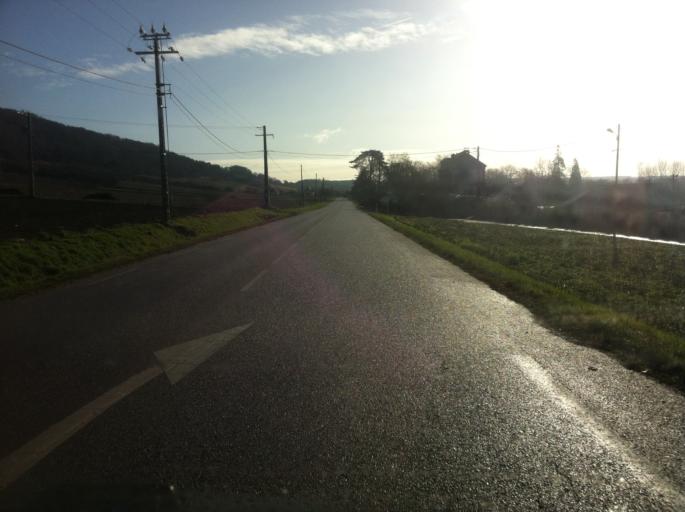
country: FR
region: Haute-Normandie
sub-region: Departement de la Seine-Maritime
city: Henouville
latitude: 49.4711
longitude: 0.9487
